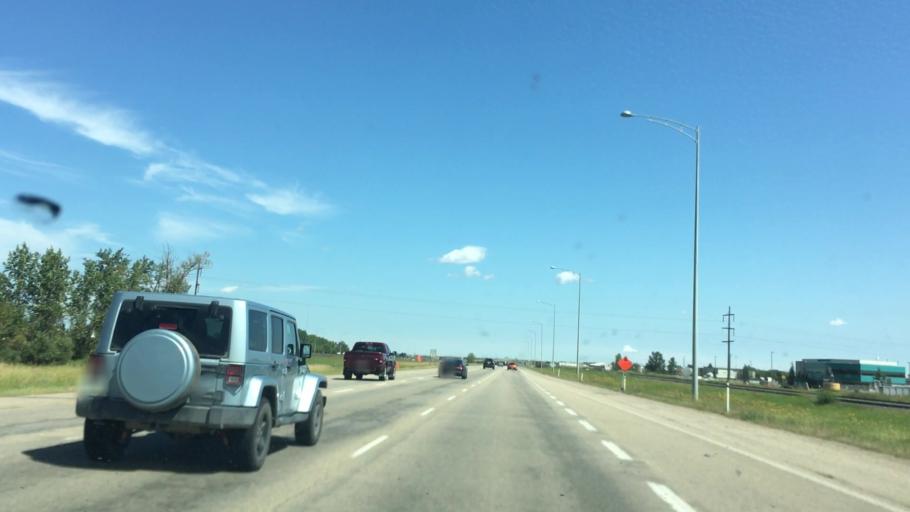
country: CA
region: Alberta
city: Leduc
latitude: 53.3655
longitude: -113.5300
